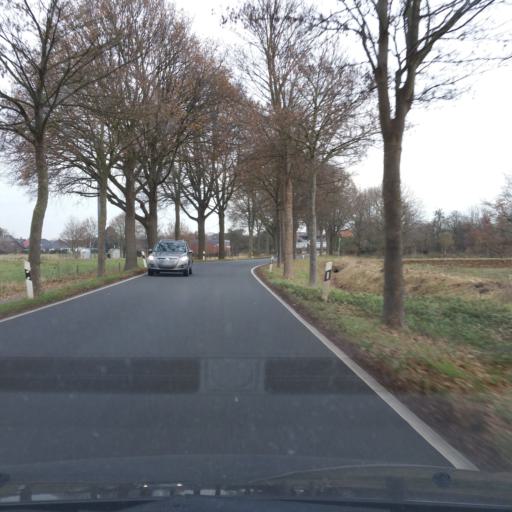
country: DE
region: North Rhine-Westphalia
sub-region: Regierungsbezirk Munster
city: Isselburg
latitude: 51.8155
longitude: 6.5048
